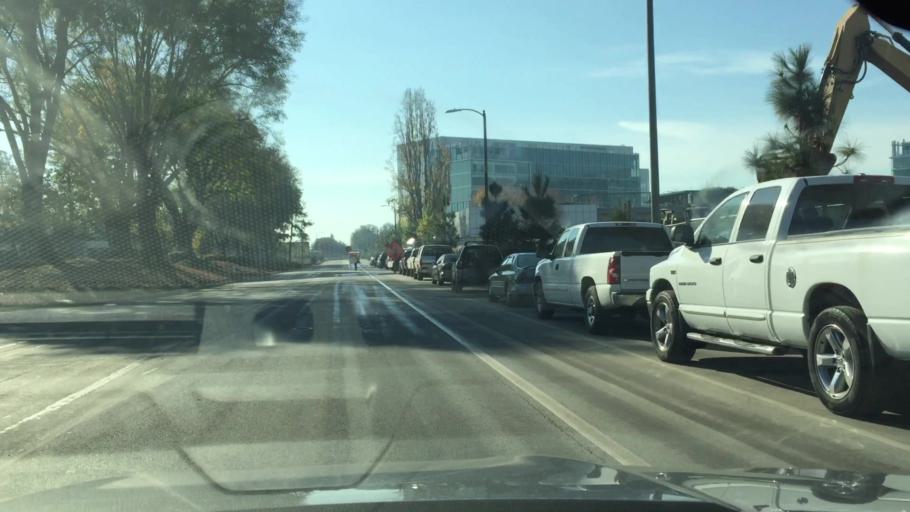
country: US
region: California
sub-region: Santa Clara County
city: Sunnyvale
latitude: 37.4084
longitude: -122.0191
